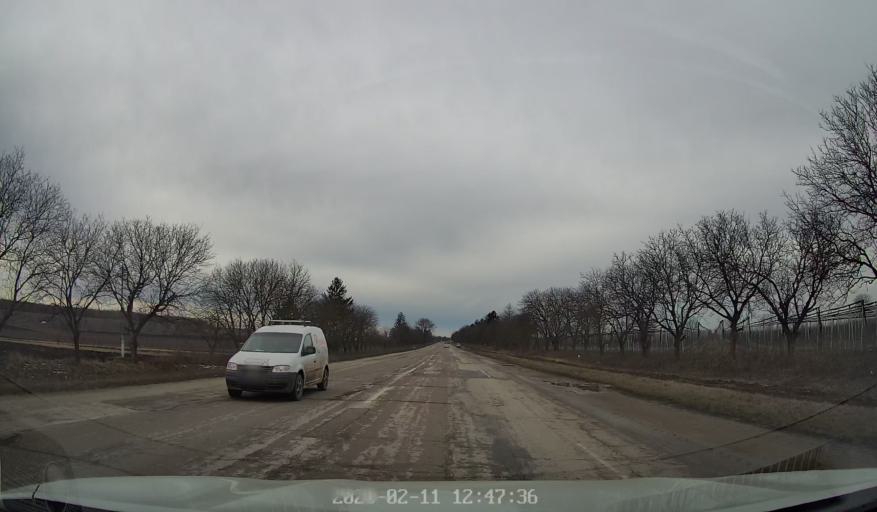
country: MD
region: Briceni
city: Briceni
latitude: 48.2733
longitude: 27.1611
